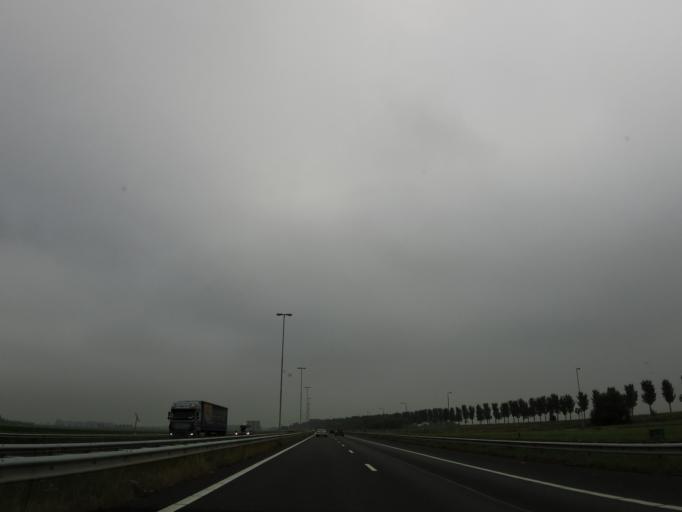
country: NL
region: North Brabant
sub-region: Gemeente Woensdrecht
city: Woensdrecht
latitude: 51.3795
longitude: 4.3028
